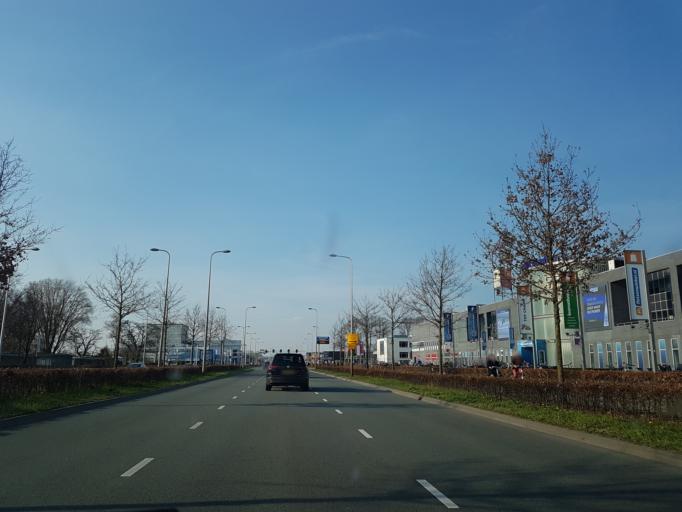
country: NL
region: Overijssel
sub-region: Gemeente Zwolle
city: Zwolle
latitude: 52.5164
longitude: 6.1195
